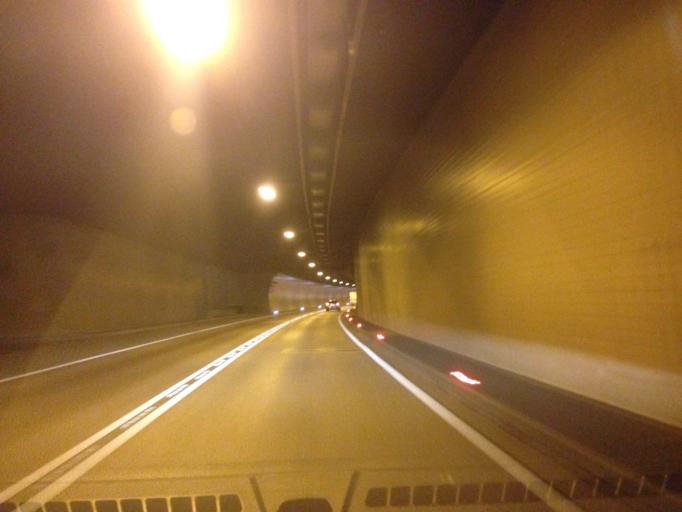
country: AT
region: Tyrol
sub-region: Politischer Bezirk Reutte
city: Lermoos
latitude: 47.4039
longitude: 10.8712
